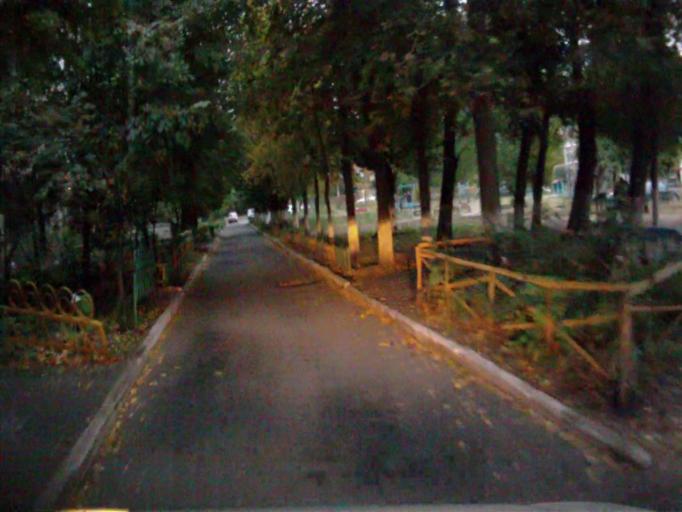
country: RU
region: Chelyabinsk
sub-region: Gorod Chelyabinsk
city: Chelyabinsk
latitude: 55.1899
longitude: 61.3364
